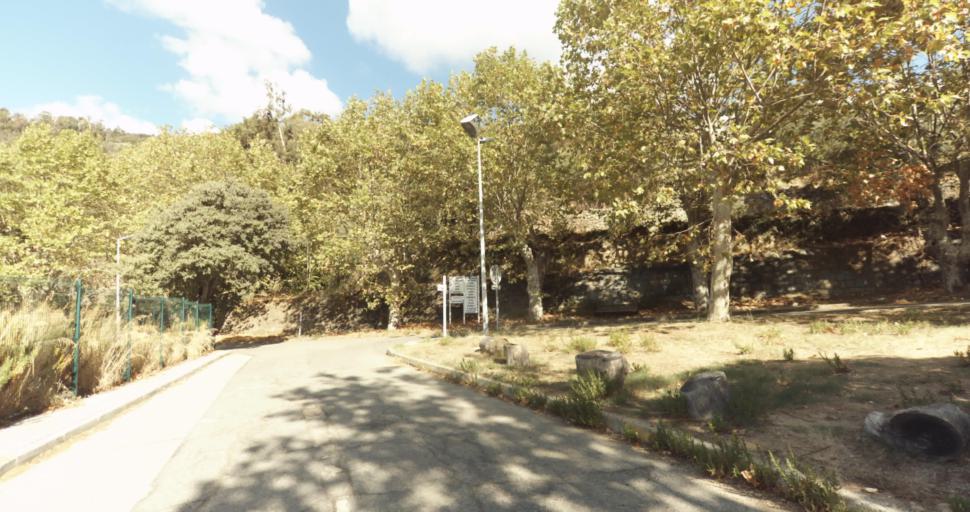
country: FR
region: Corsica
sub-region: Departement de la Corse-du-Sud
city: Ajaccio
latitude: 41.9356
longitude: 8.7144
